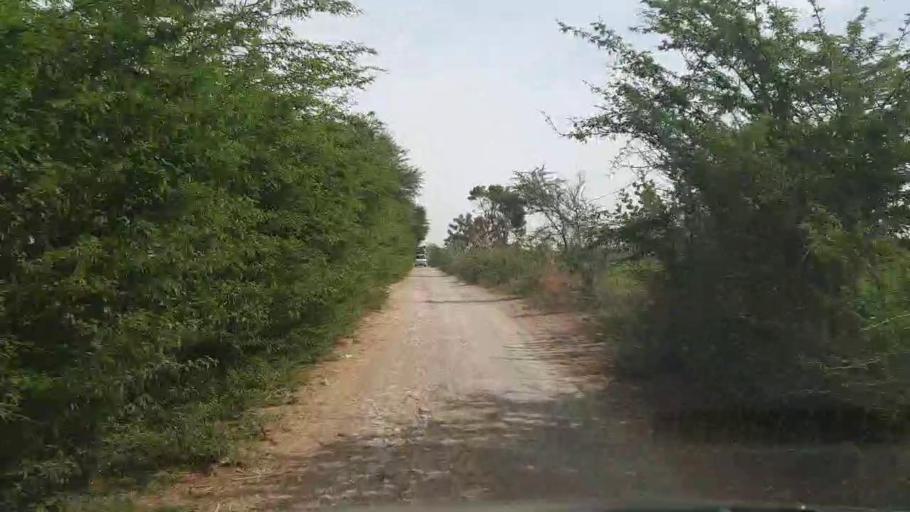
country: PK
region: Sindh
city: Umarkot
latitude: 25.2519
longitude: 69.7058
